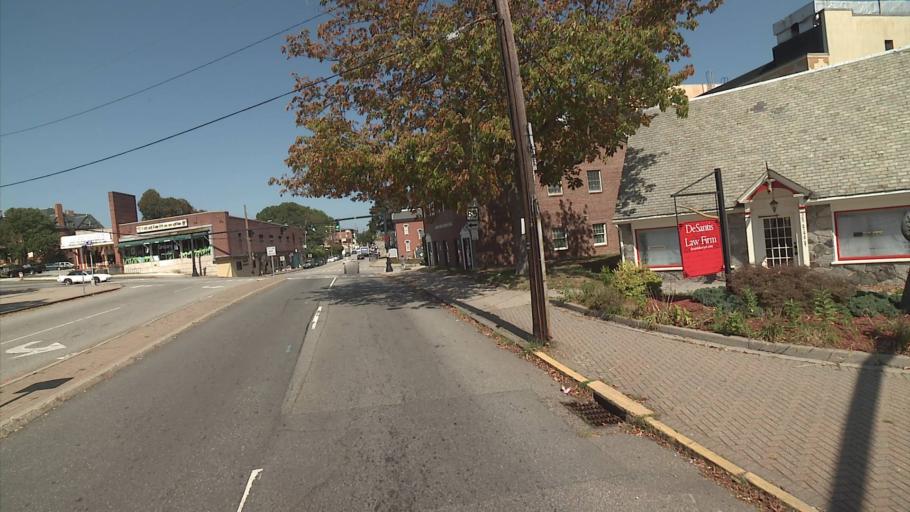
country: US
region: Connecticut
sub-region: New London County
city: New London
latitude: 41.3553
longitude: -72.0995
